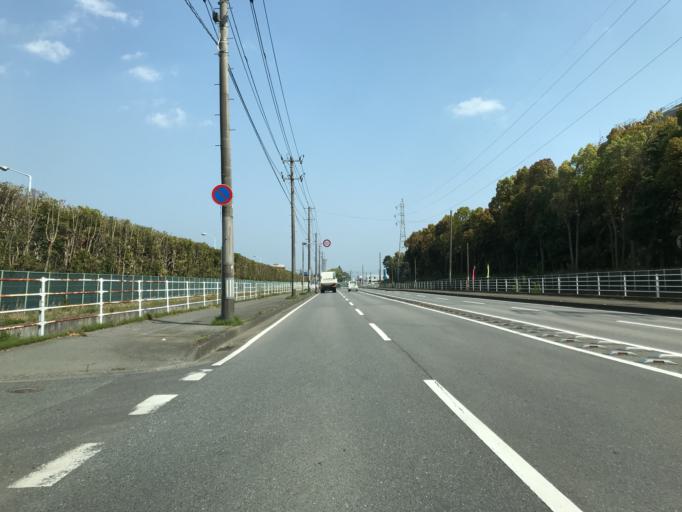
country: JP
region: Ibaraki
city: Kitaibaraki
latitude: 36.8981
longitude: 140.7728
